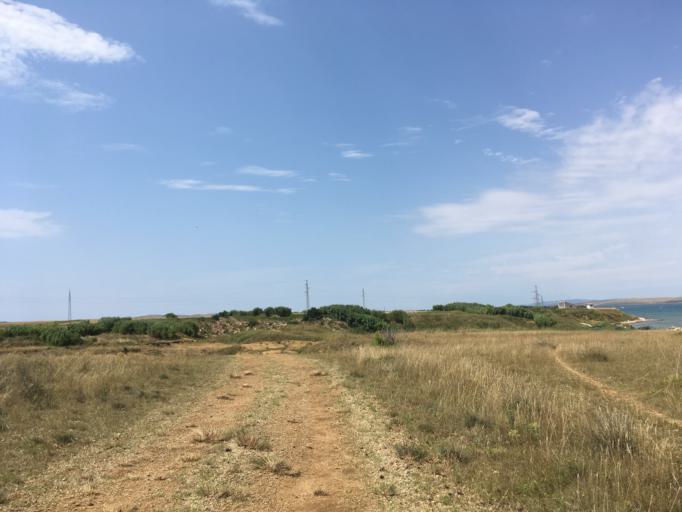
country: HR
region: Zadarska
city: Privlaka
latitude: 44.2732
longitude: 15.1483
